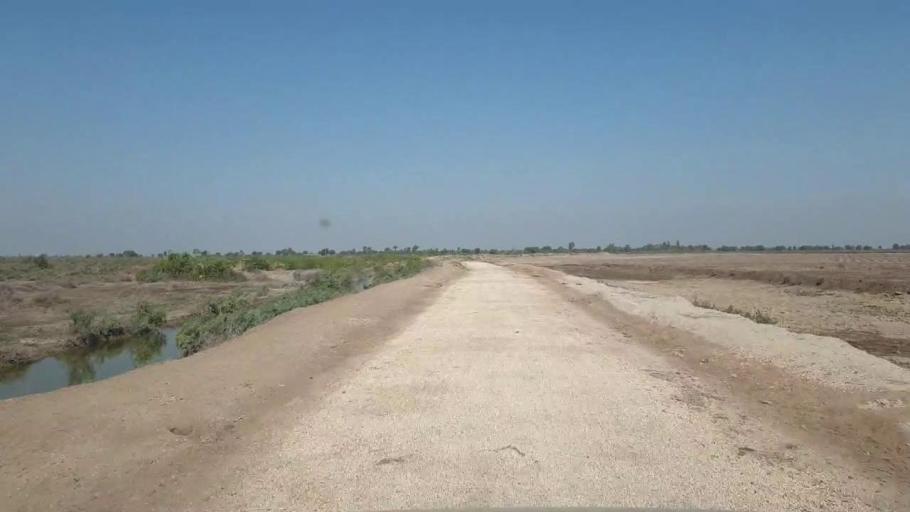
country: PK
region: Sindh
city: Digri
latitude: 25.2410
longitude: 69.2025
